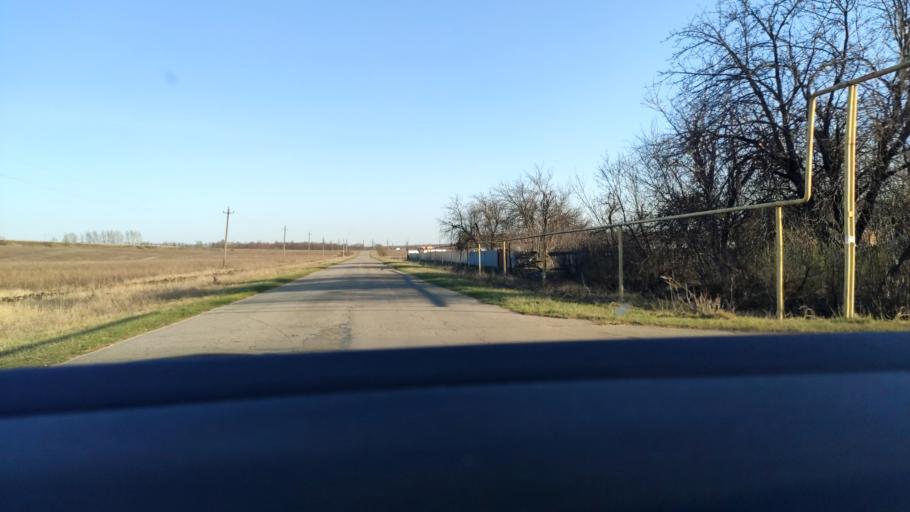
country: RU
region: Voronezj
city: Uryv-Pokrovka
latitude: 51.1377
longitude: 39.0419
